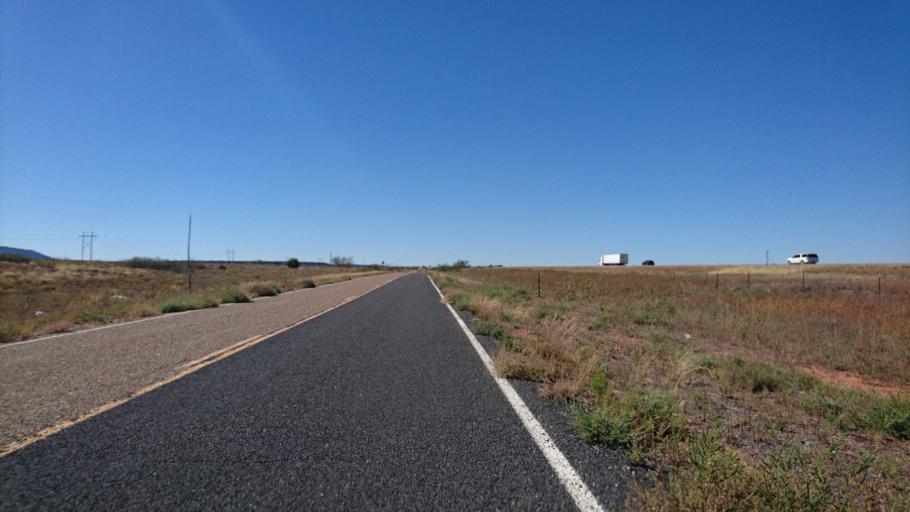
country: US
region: New Mexico
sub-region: Quay County
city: Tucumcari
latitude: 35.0864
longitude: -104.0970
